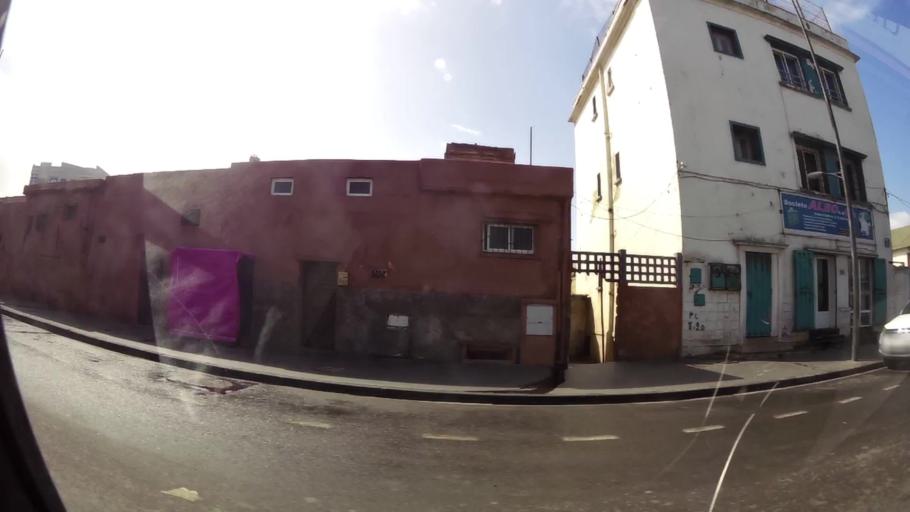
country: MA
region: Grand Casablanca
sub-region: Mediouna
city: Tit Mellil
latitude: 33.6194
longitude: -7.5359
